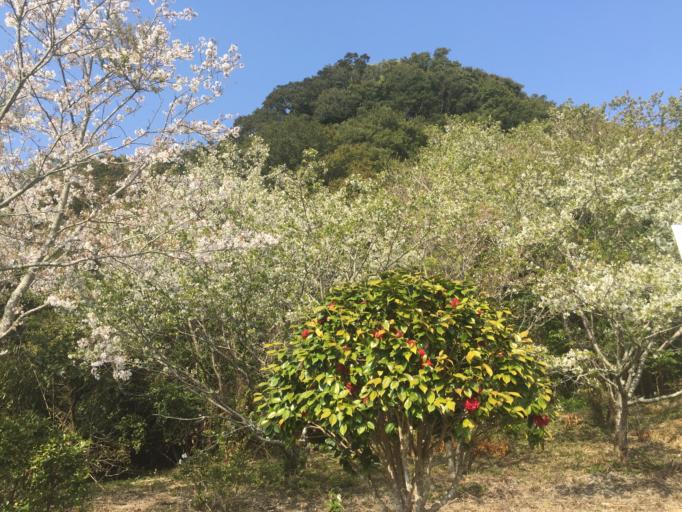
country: JP
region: Shizuoka
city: Kakegawa
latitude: 34.6722
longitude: 138.0354
